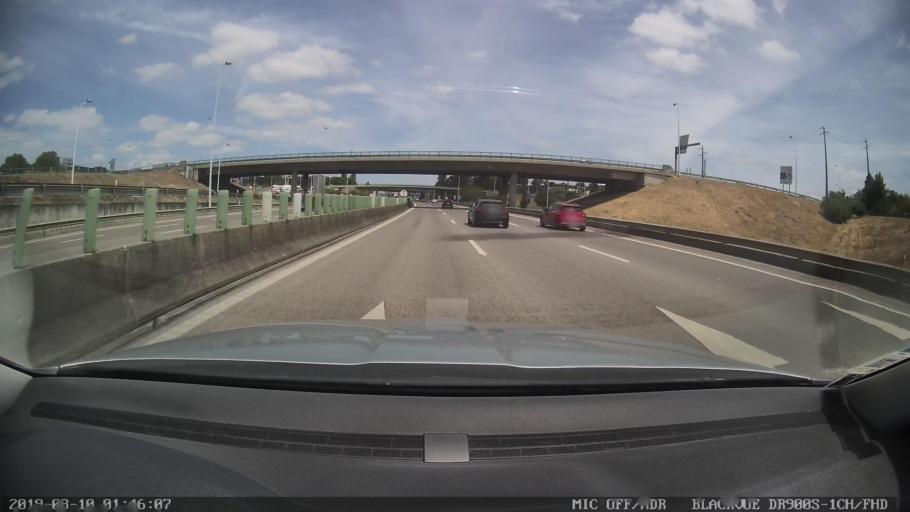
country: PT
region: Lisbon
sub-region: Vila Franca de Xira
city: Vialonga
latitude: 38.8928
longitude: -9.0546
